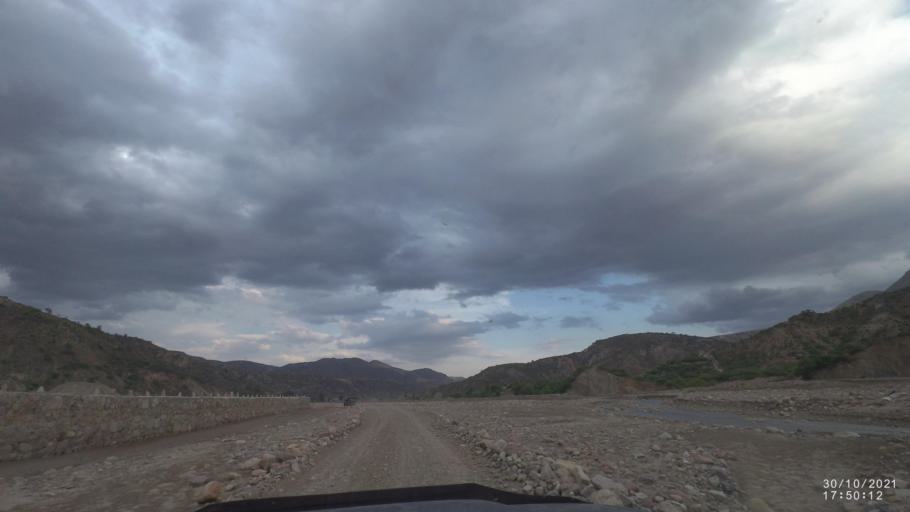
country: BO
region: Cochabamba
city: Sipe Sipe
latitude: -17.5364
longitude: -66.5113
